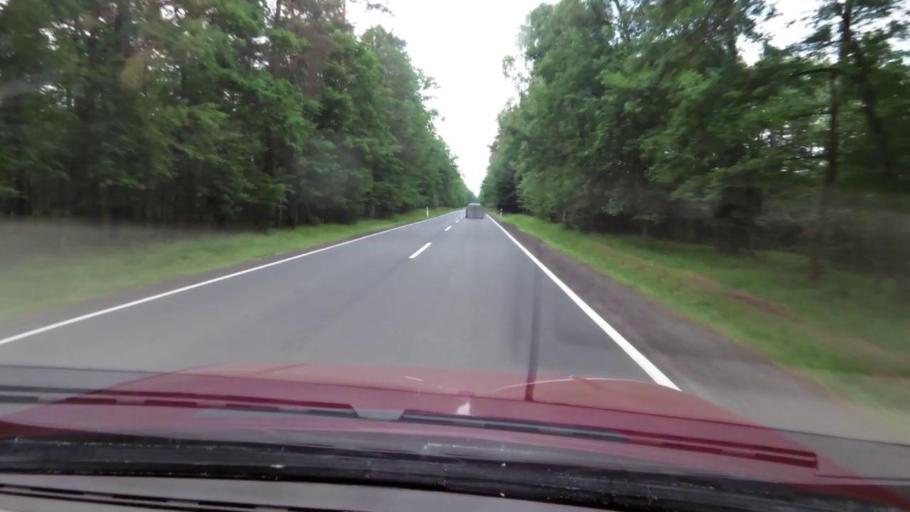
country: PL
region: Pomeranian Voivodeship
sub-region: Powiat bytowski
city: Trzebielino
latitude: 54.2221
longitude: 17.0878
